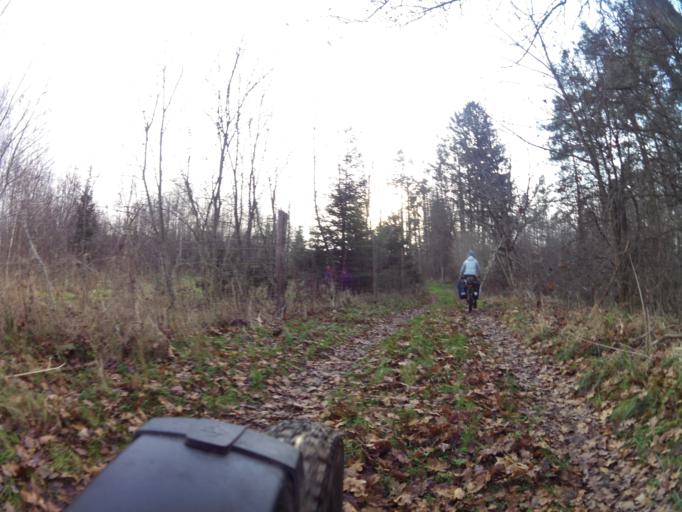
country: PL
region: West Pomeranian Voivodeship
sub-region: Powiat koszalinski
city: Polanow
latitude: 54.1983
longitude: 16.7247
